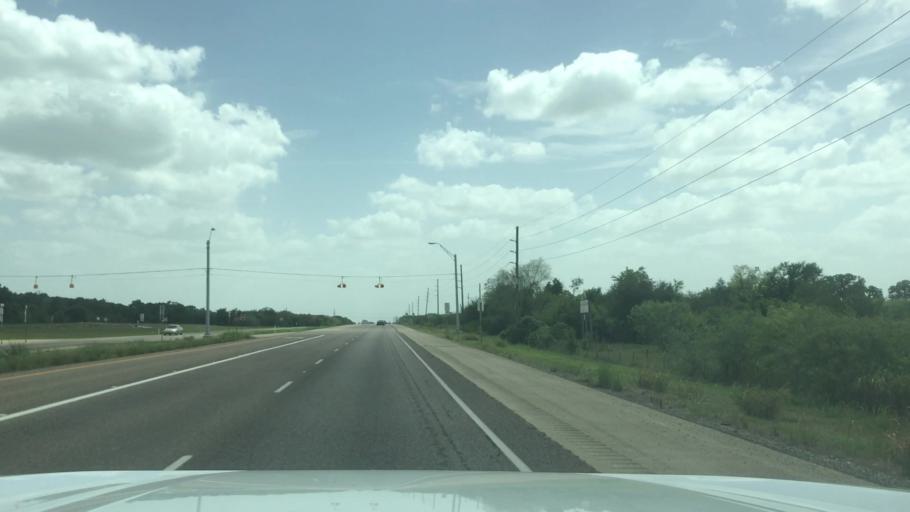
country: US
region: Texas
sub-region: Robertson County
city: Calvert
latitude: 31.1157
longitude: -96.7122
